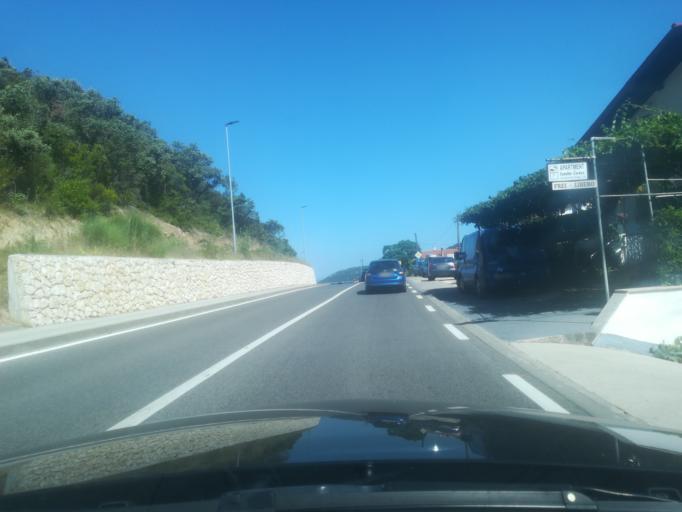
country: HR
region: Primorsko-Goranska
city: Supetarska Draga
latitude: 44.7930
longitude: 14.7317
